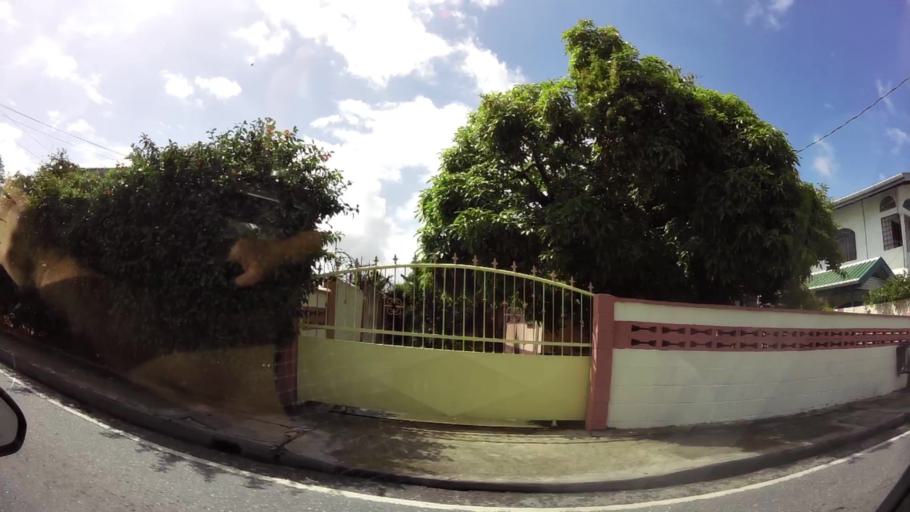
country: TT
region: Borough of Arima
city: Arima
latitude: 10.6365
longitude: -61.2765
